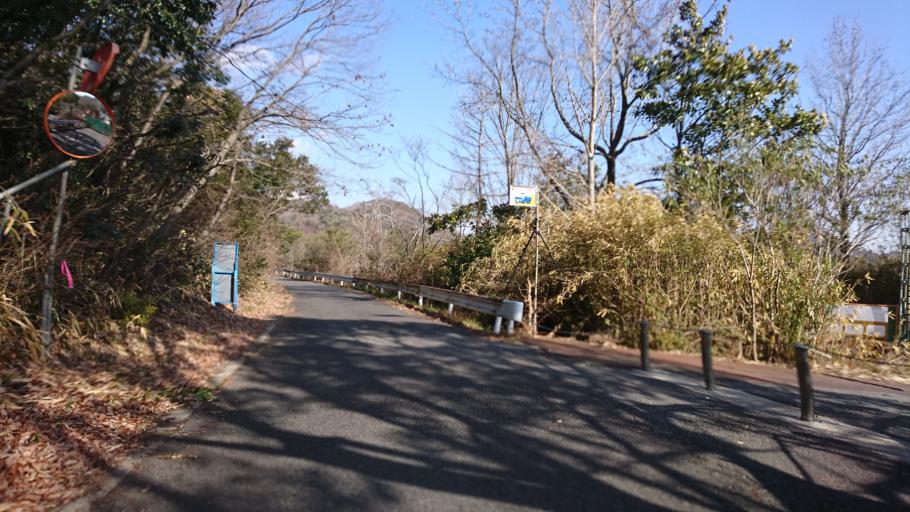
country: JP
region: Hyogo
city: Ono
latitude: 34.8267
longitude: 134.8732
